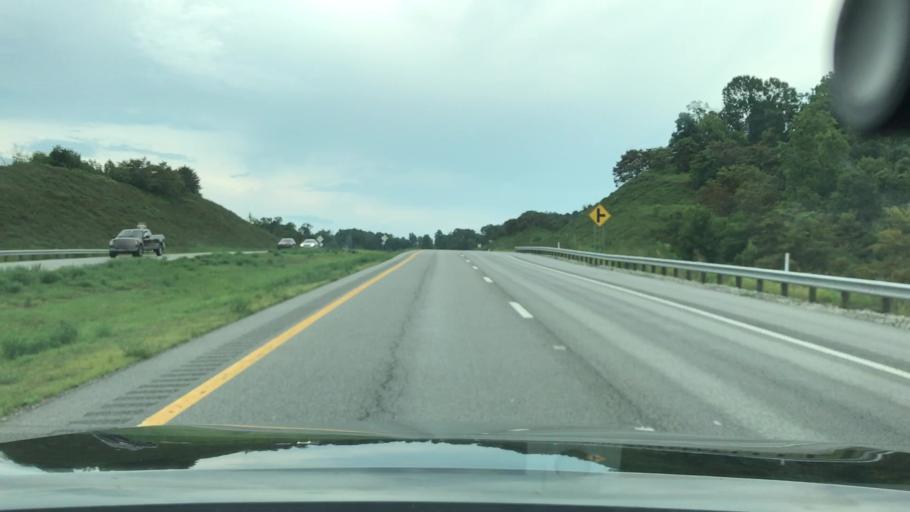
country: US
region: West Virginia
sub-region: Mason County
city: Point Pleasant
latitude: 38.7945
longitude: -82.0965
